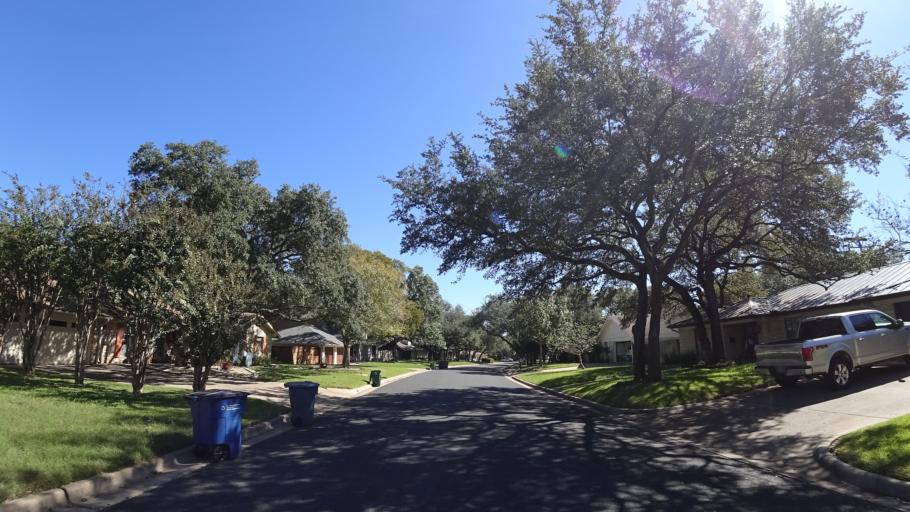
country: US
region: Texas
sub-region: Williamson County
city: Jollyville
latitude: 30.3674
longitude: -97.7617
